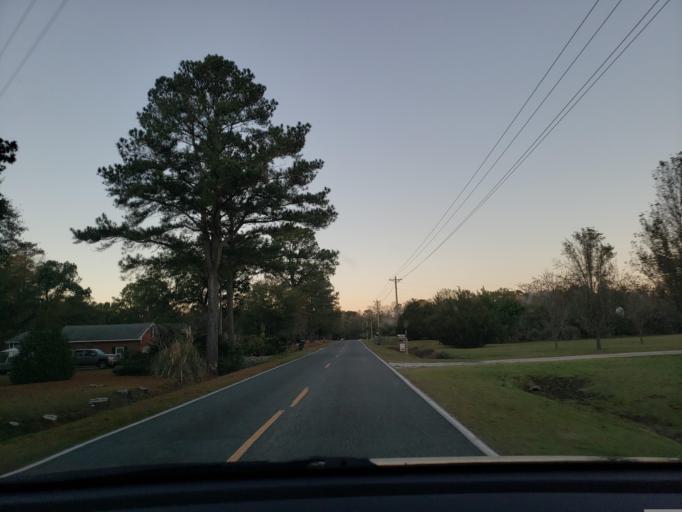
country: US
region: North Carolina
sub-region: Onslow County
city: Richlands
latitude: 34.7535
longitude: -77.6543
